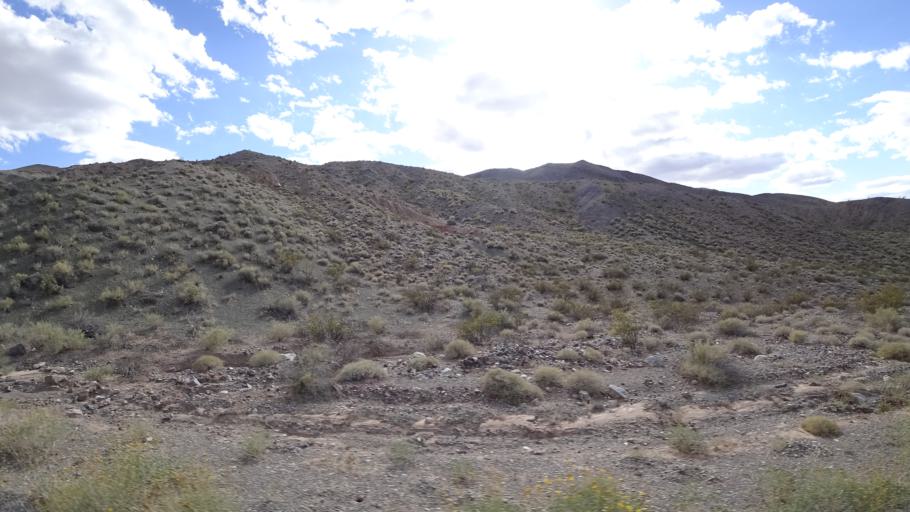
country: US
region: Nevada
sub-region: Nye County
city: Beatty
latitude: 36.4364
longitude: -117.1952
